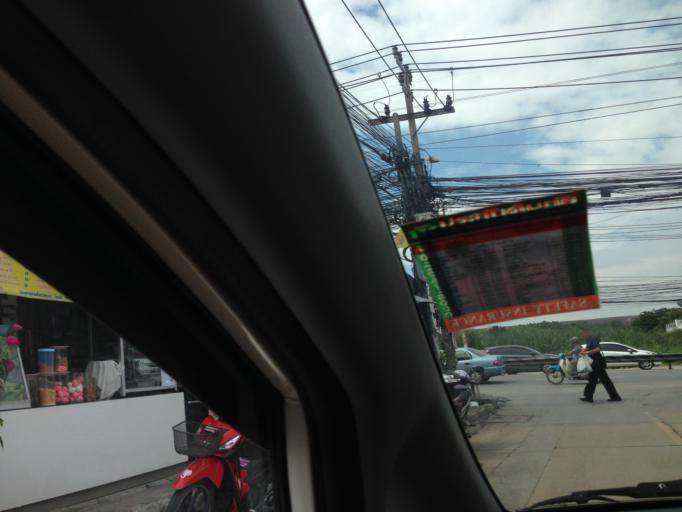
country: TH
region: Nonthaburi
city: Pak Kret
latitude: 13.9369
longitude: 100.5394
